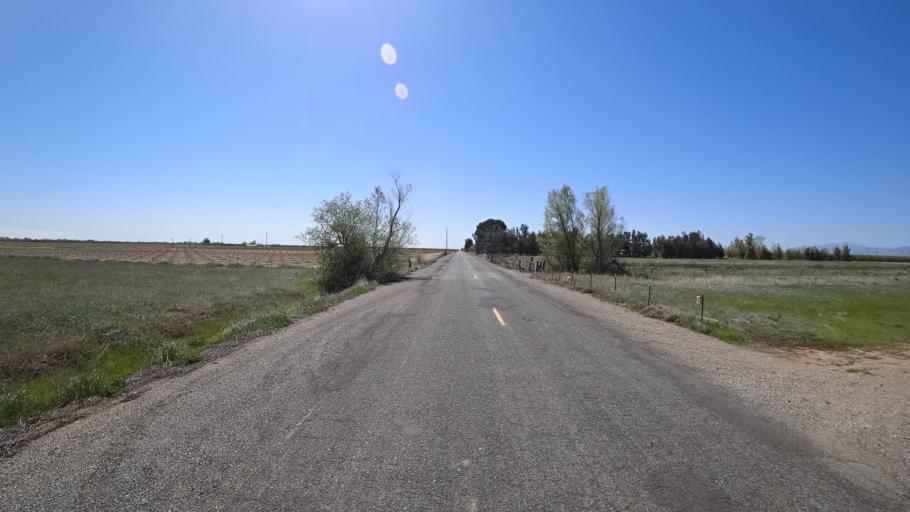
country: US
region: California
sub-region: Glenn County
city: Orland
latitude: 39.6830
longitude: -122.2531
